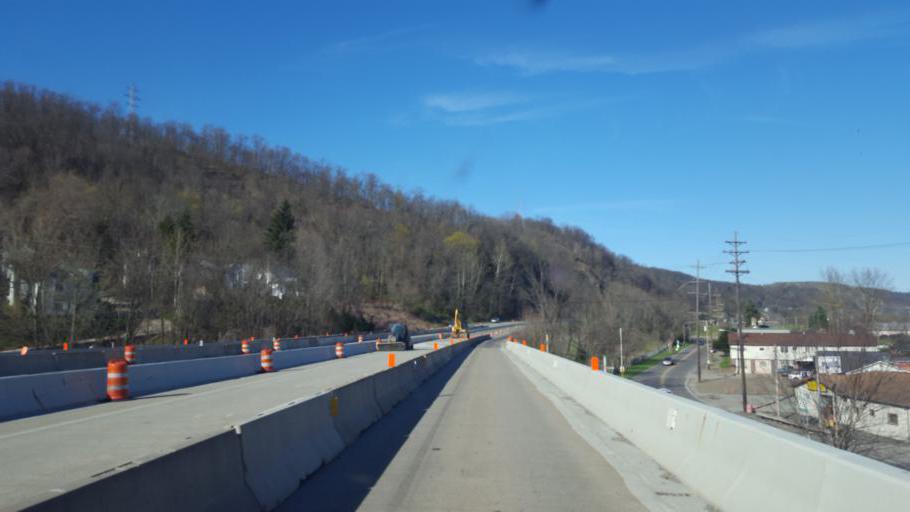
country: US
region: Ohio
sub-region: Columbiana County
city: Wellsville
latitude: 40.6142
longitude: -80.6419
